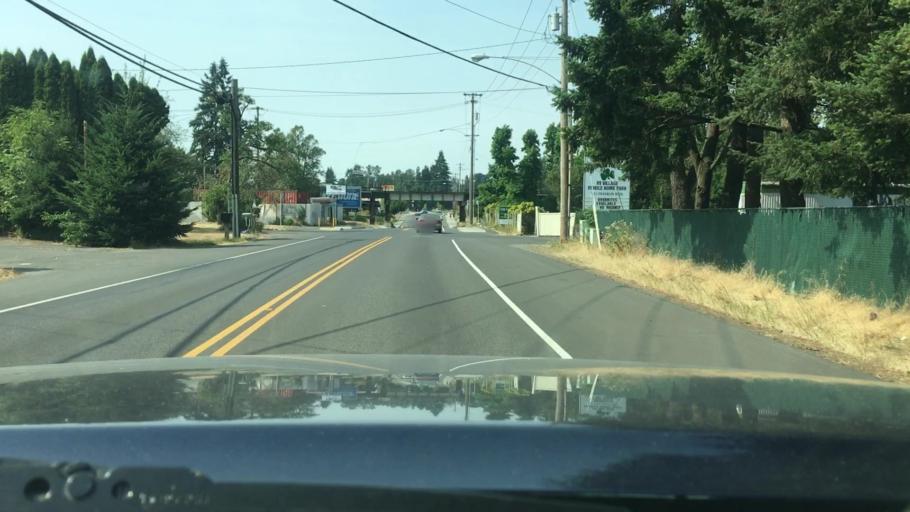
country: US
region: Oregon
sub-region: Lane County
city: Springfield
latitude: 44.0405
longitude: -123.0288
